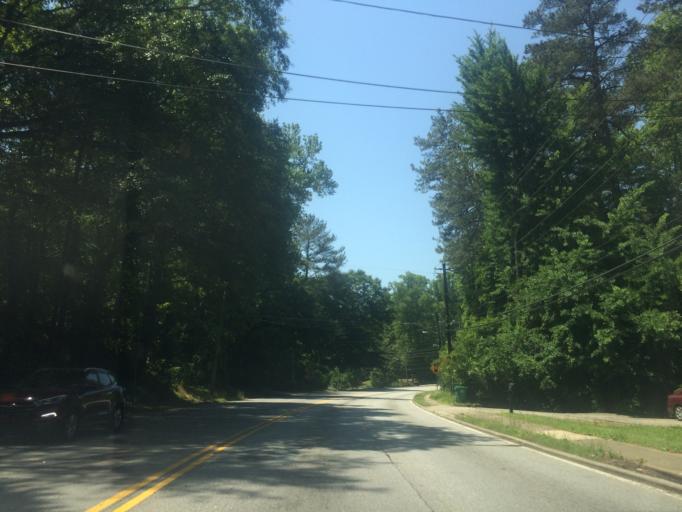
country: US
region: Georgia
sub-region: DeKalb County
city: Decatur
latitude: 33.7754
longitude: -84.3120
